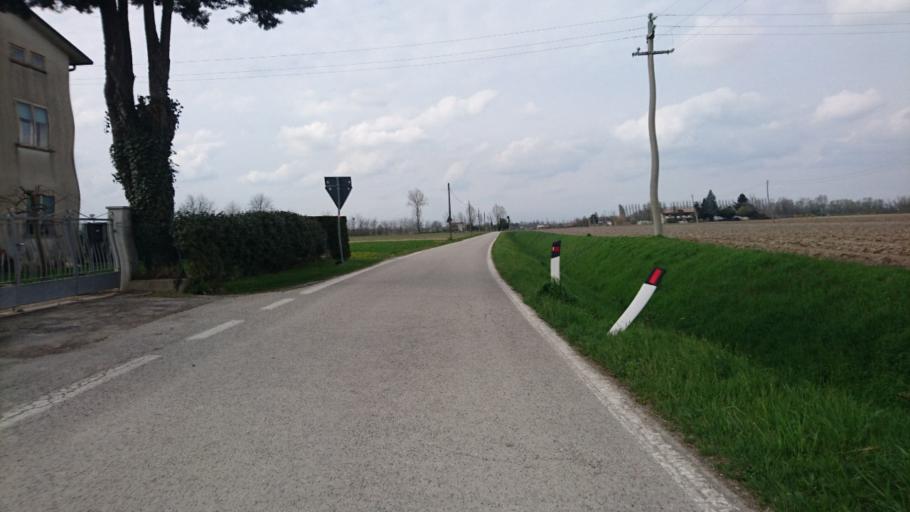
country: IT
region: Veneto
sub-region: Provincia di Padova
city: Tremignon
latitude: 45.5249
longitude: 11.8095
